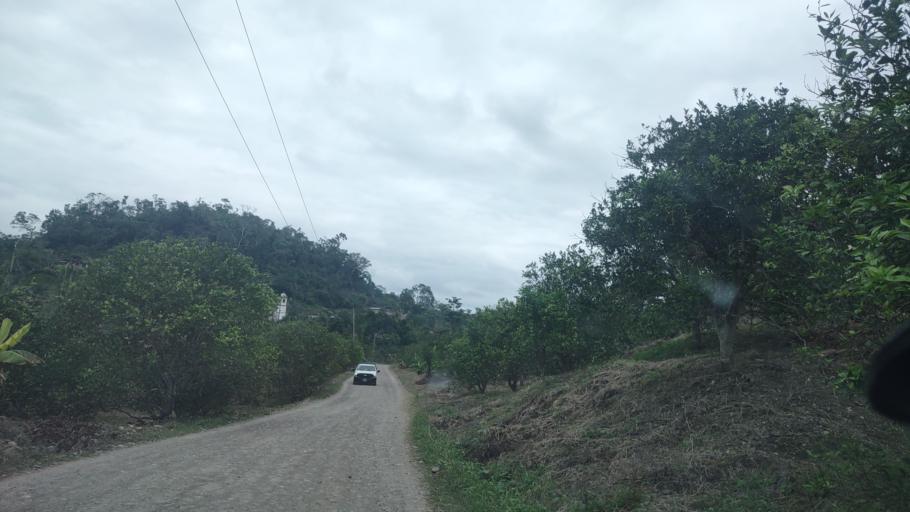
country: MX
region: Veracruz
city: Papantla de Olarte
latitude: 20.4321
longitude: -97.2646
